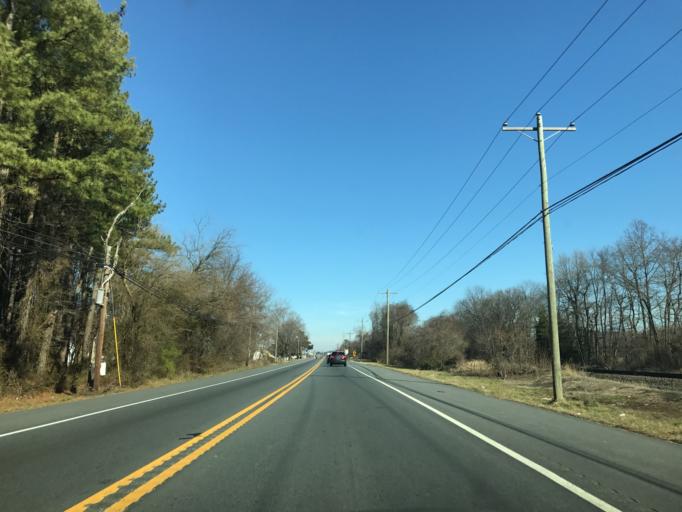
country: US
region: Delaware
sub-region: New Castle County
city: Middletown
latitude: 39.5003
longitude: -75.7130
